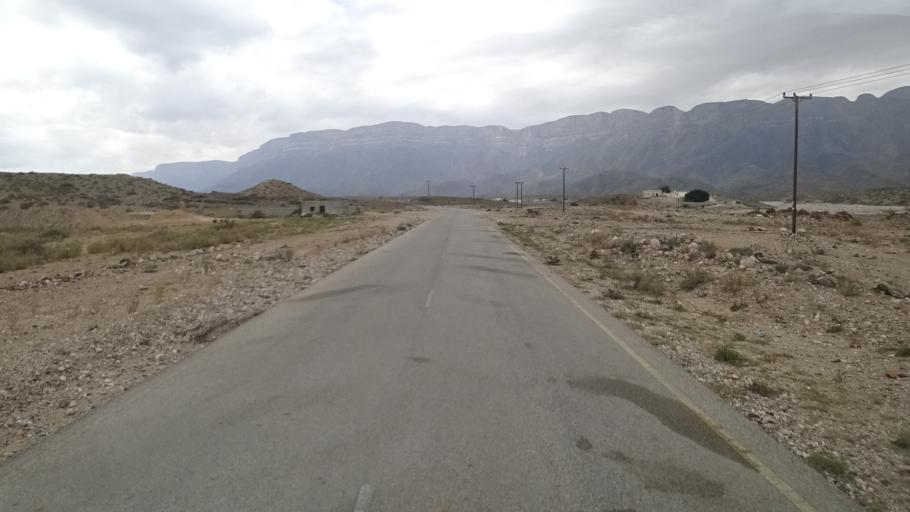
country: OM
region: Zufar
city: Salalah
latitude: 17.1607
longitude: 54.9926
